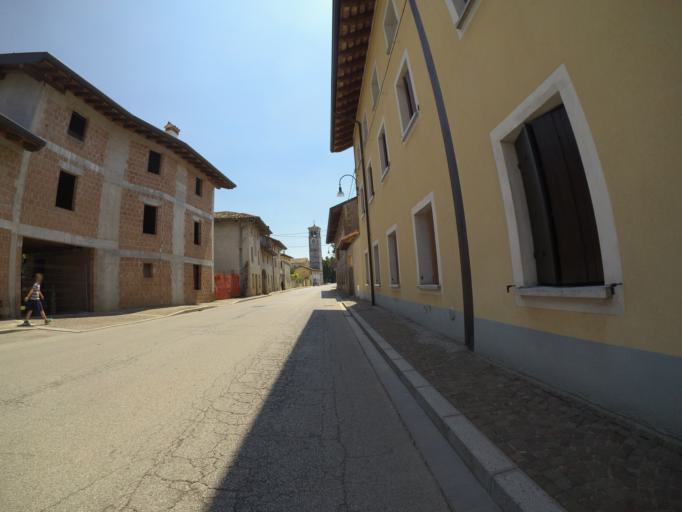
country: IT
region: Friuli Venezia Giulia
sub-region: Provincia di Udine
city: Lestizza
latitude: 45.9772
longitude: 13.1386
